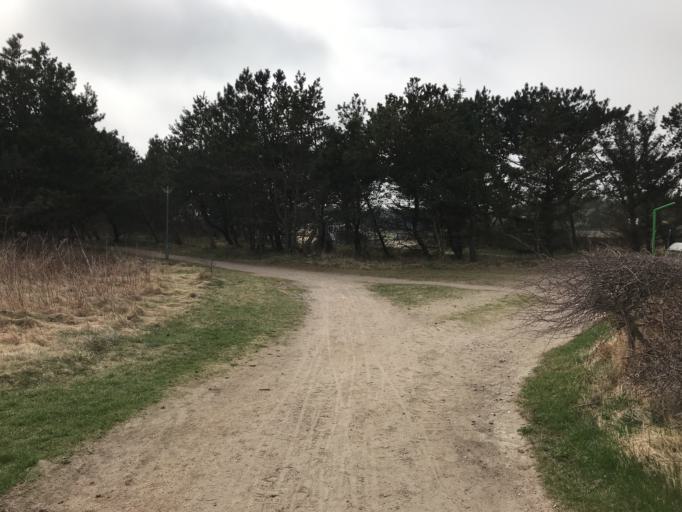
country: DK
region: North Denmark
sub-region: Hjorring Kommune
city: Hjorring
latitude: 57.4929
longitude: 9.8376
